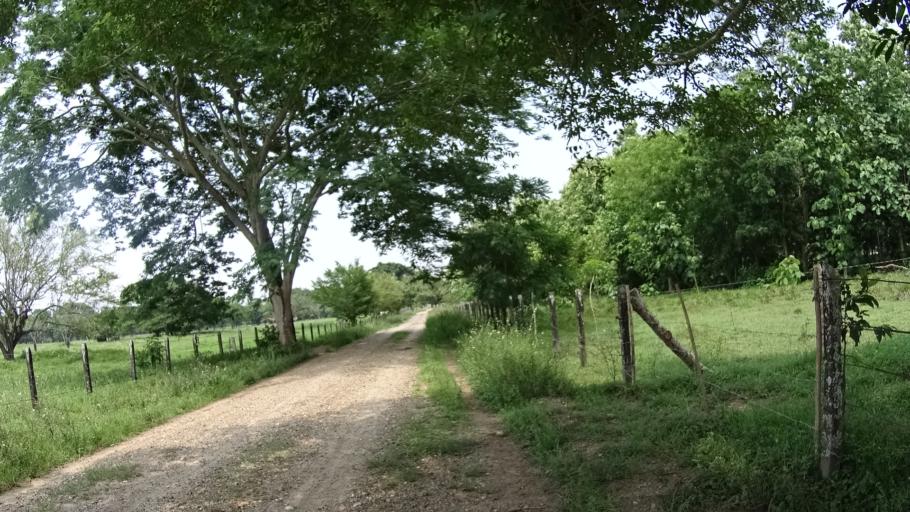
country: CO
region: Cundinamarca
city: Puerto Salgar
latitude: 5.5464
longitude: -74.6607
